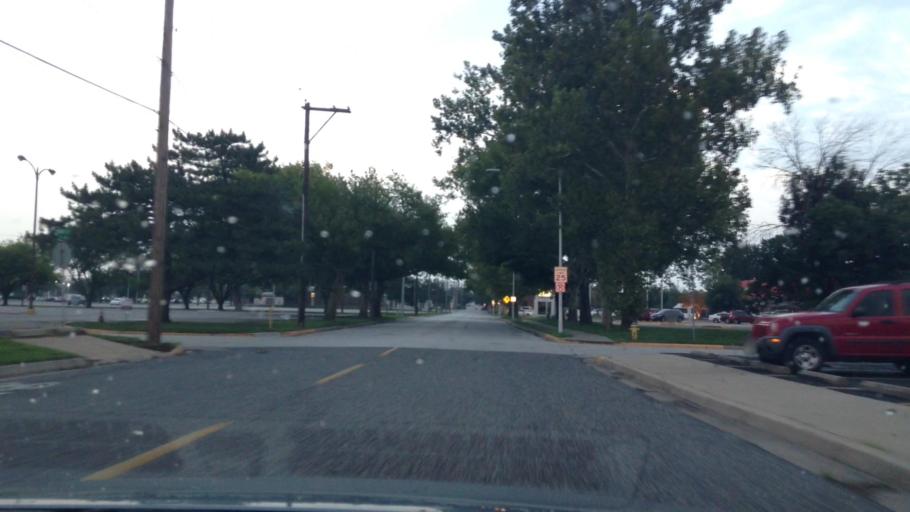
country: US
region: Missouri
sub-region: Clay County
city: North Kansas City
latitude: 39.1402
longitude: -94.5764
